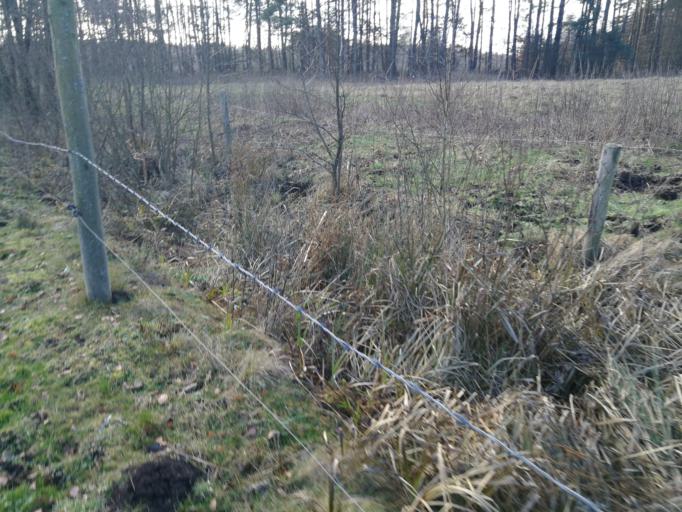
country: PL
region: Warmian-Masurian Voivodeship
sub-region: Powiat dzialdowski
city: Rybno
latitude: 53.4133
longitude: 19.9080
